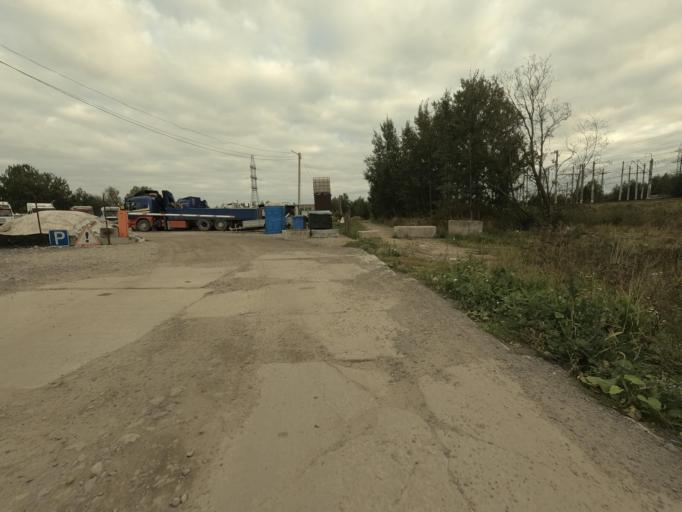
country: RU
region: St.-Petersburg
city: Petro-Slavyanka
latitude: 59.8220
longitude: 30.5275
